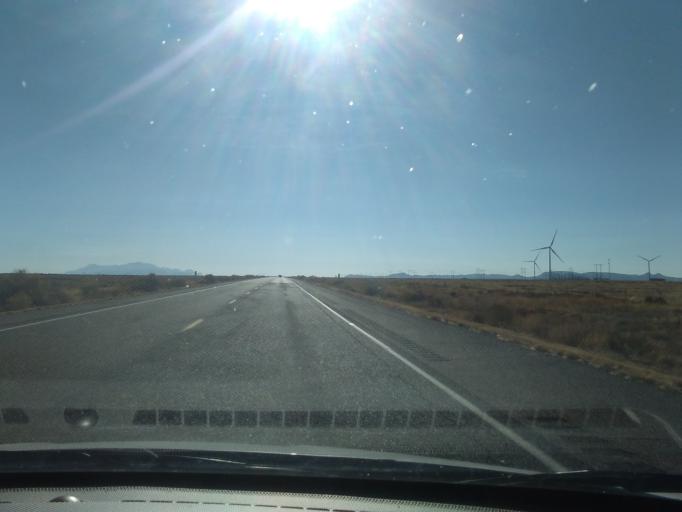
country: US
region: New Mexico
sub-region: Dona Ana County
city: Hatch
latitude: 32.5460
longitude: -107.4798
